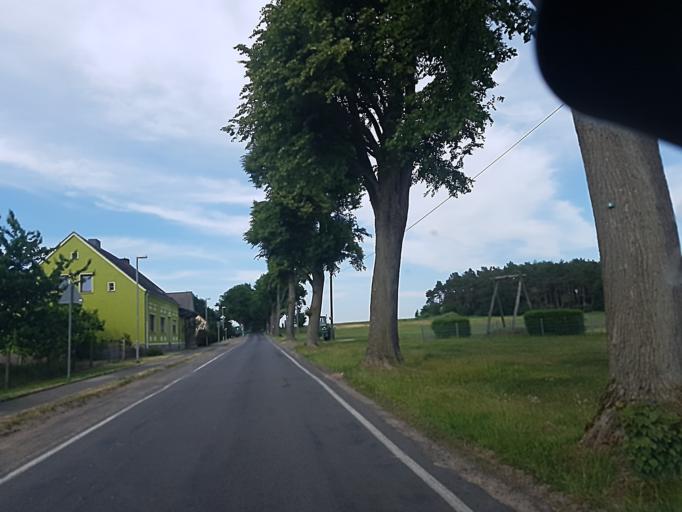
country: DE
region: Saxony-Anhalt
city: Nudersdorf
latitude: 52.0157
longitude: 12.6145
